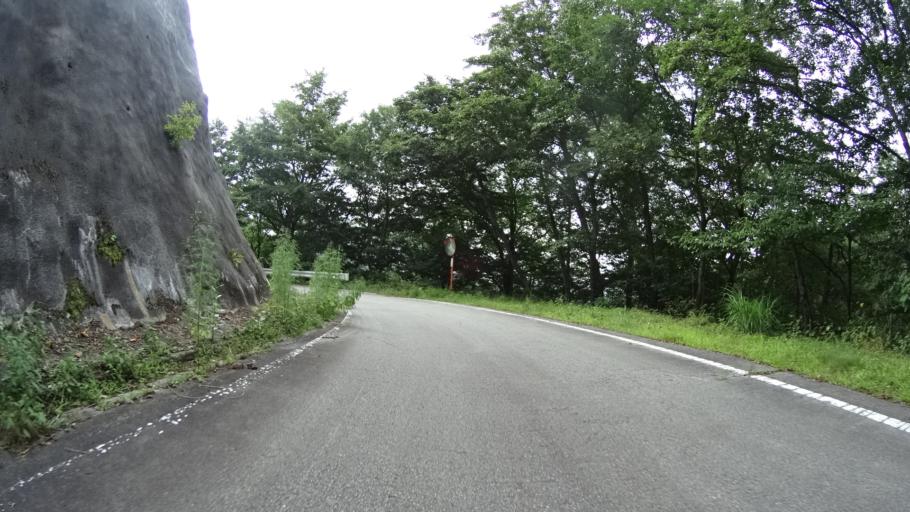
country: JP
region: Yamanashi
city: Nirasaki
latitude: 35.8074
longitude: 138.5424
